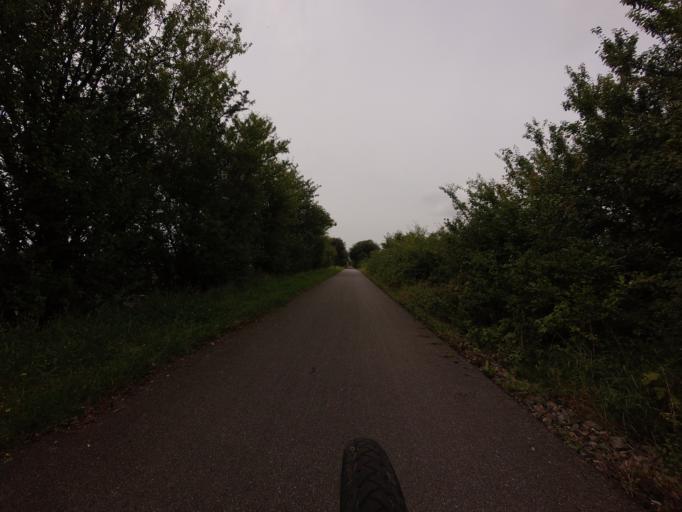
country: DK
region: Zealand
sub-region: Naestved Kommune
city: Fuglebjerg
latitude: 55.2635
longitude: 11.5375
